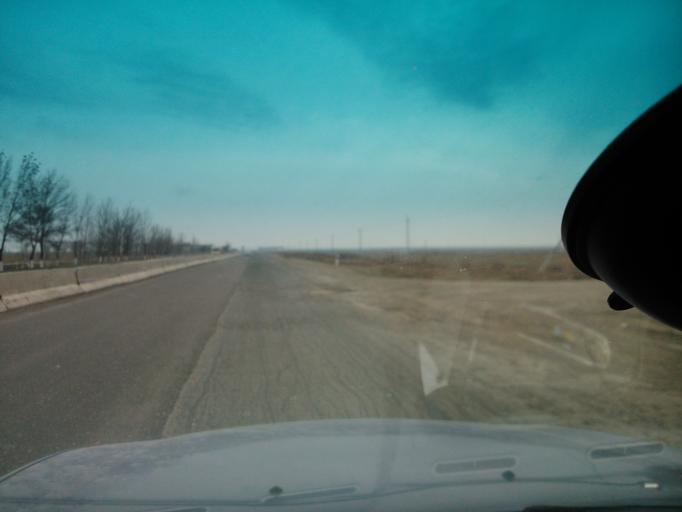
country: UZ
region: Sirdaryo
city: Yangiyer
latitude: 40.3779
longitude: 68.7974
